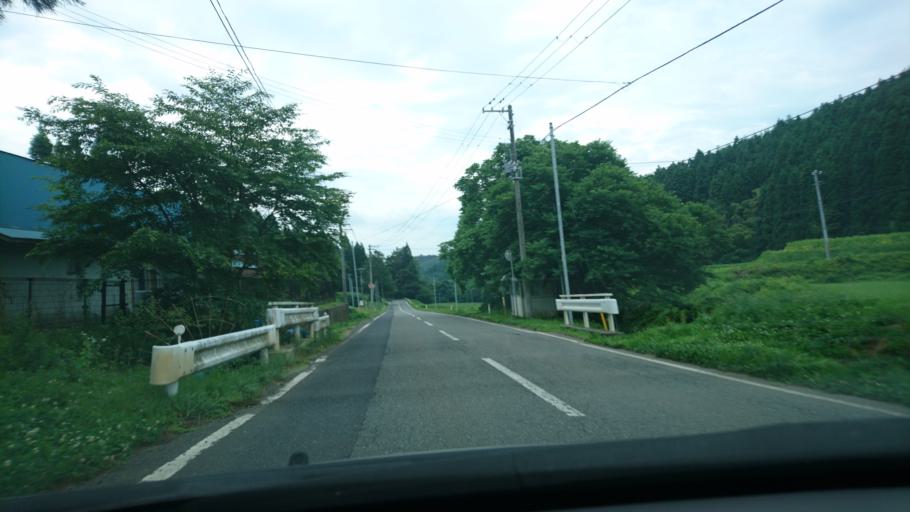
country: JP
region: Iwate
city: Ichinoseki
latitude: 38.8776
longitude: 141.4266
